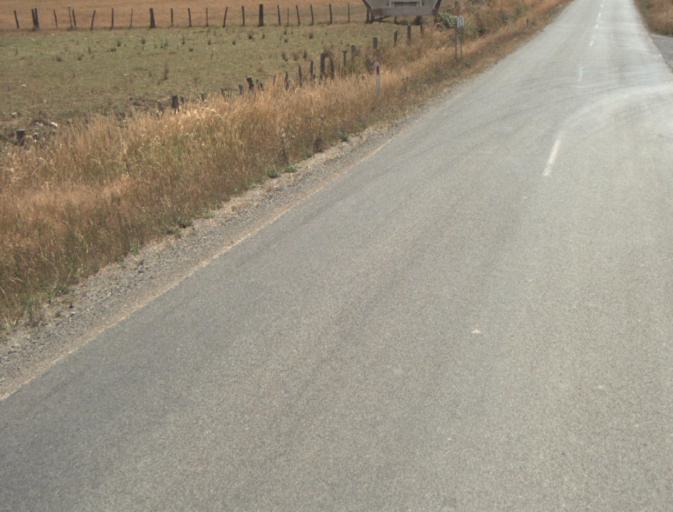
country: AU
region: Tasmania
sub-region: Dorset
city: Scottsdale
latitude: -41.2869
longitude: 147.3841
